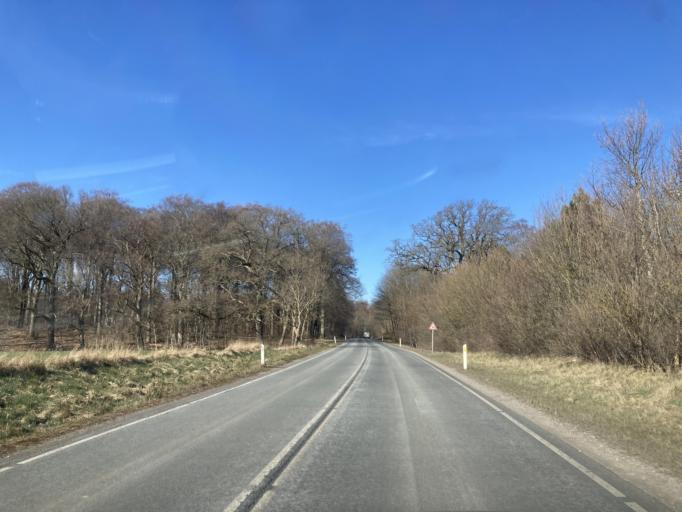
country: DK
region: Capital Region
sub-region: Gribskov Kommune
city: Graested
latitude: 56.0337
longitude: 12.2815
